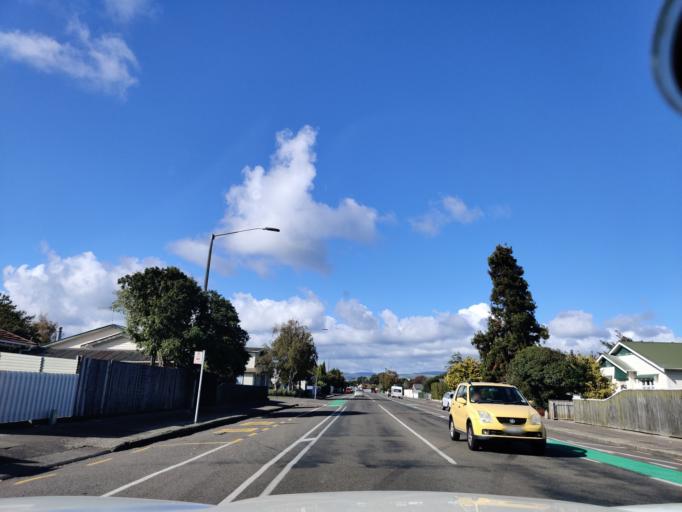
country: NZ
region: Manawatu-Wanganui
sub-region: Palmerston North City
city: Palmerston North
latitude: -40.3504
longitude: 175.5977
